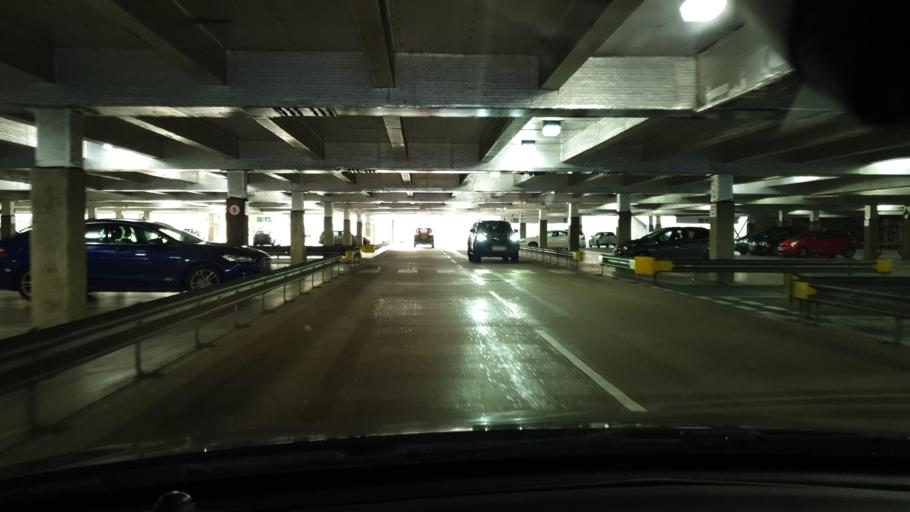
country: GB
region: England
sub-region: City and Borough of Birmingham
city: Birmingham
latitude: 52.5031
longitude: -1.8542
